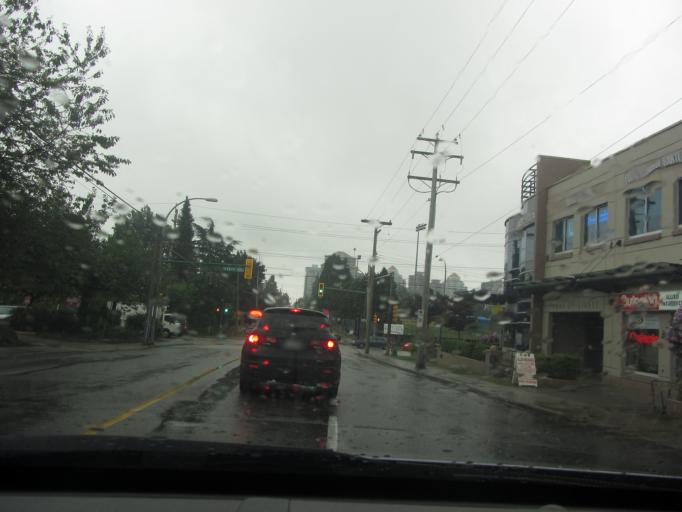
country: CA
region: British Columbia
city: New Westminster
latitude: 49.2193
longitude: -122.9282
